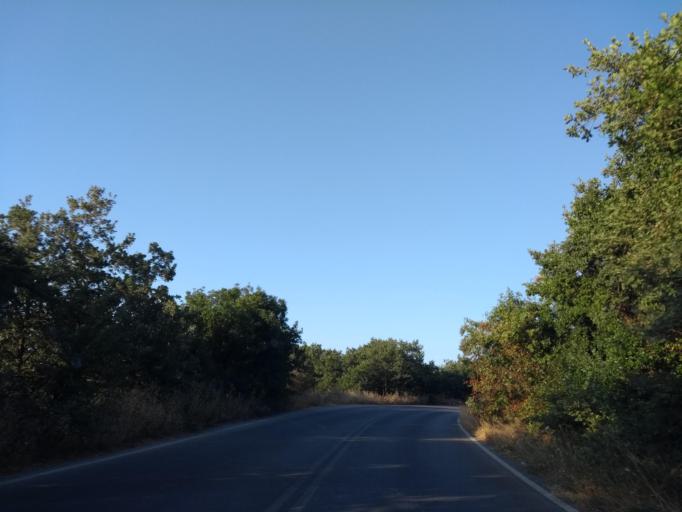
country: GR
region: Crete
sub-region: Nomos Chanias
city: Kalivai
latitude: 35.4089
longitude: 24.2070
